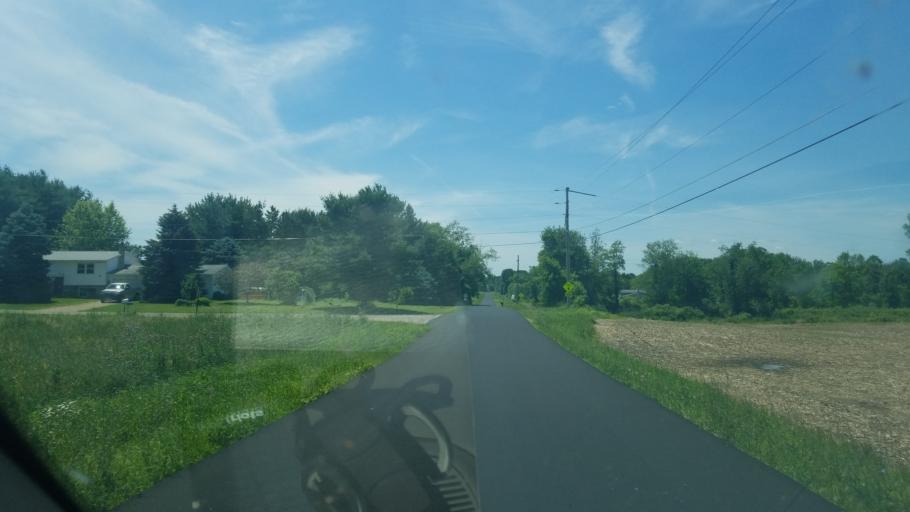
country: US
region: Ohio
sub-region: Stark County
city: Alliance
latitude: 40.8578
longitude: -81.1471
